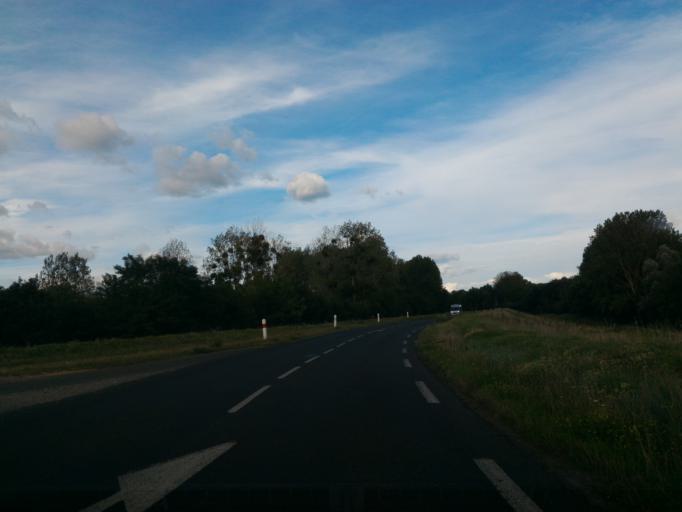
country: FR
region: Centre
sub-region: Departement du Loir-et-Cher
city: Montlivault
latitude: 47.6503
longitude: 1.4463
